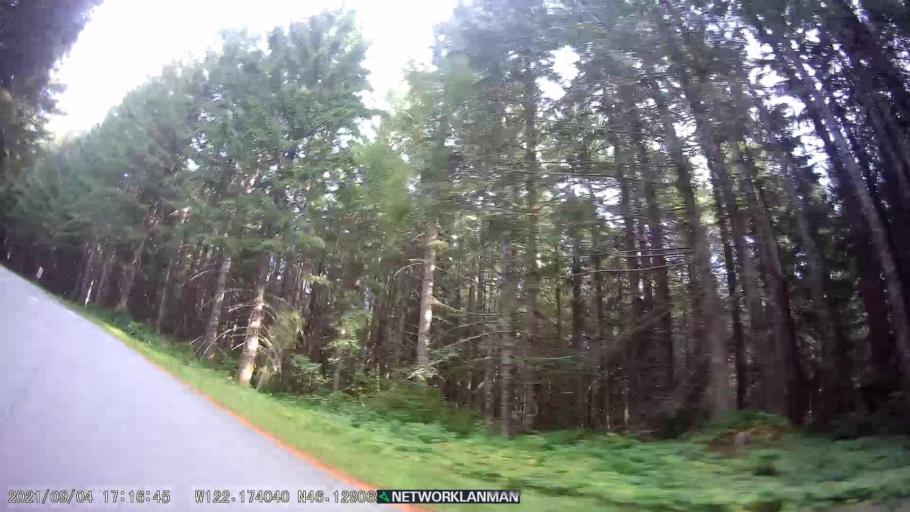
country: US
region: Washington
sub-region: Clark County
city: Amboy
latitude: 46.1289
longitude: -122.1738
